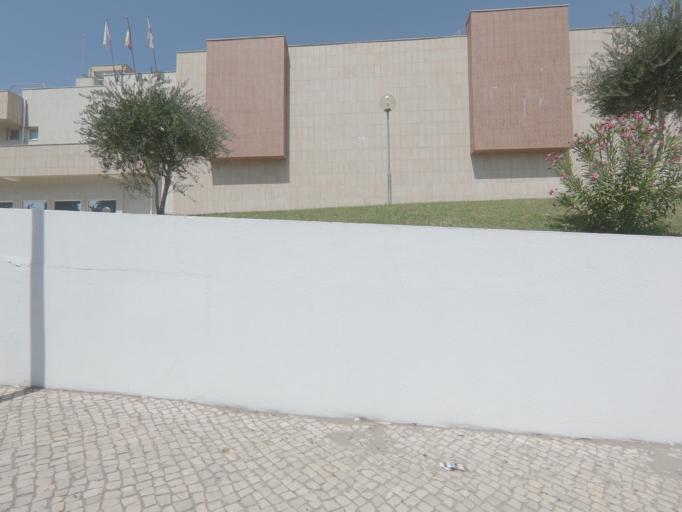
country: PT
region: Setubal
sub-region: Setubal
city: Setubal
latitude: 38.5326
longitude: -8.9096
